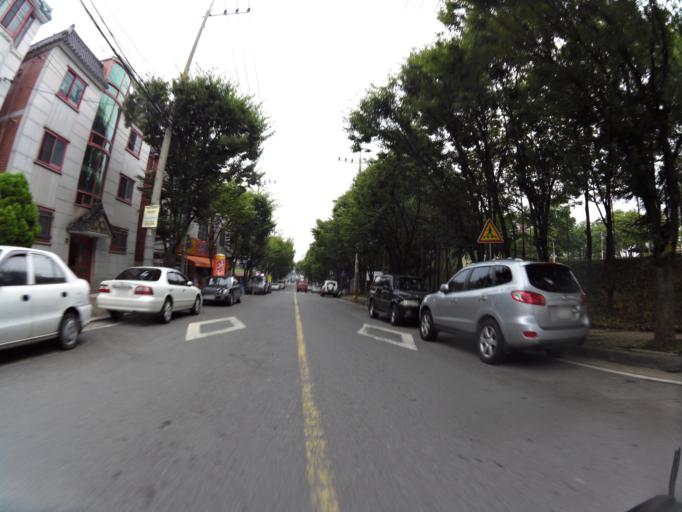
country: KR
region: Gyeongsangbuk-do
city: Gyeongsan-si
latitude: 35.8420
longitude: 128.7528
